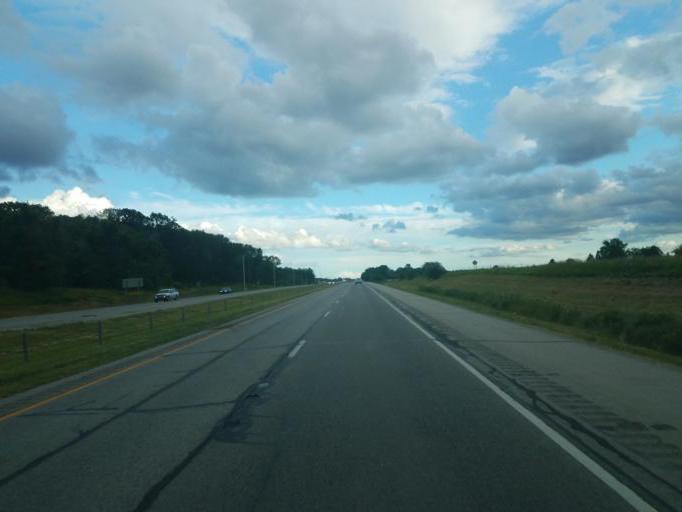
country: US
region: Indiana
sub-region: DeKalb County
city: Garrett
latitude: 41.3063
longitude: -85.0878
